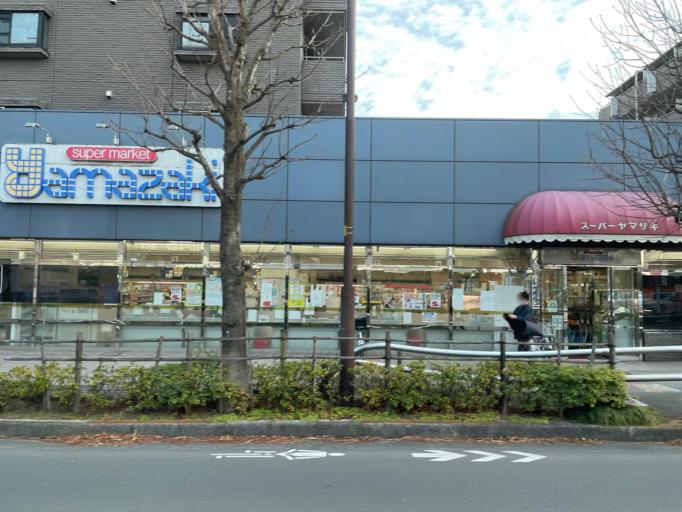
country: JP
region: Tokyo
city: Tanashicho
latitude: 35.7596
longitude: 139.5319
